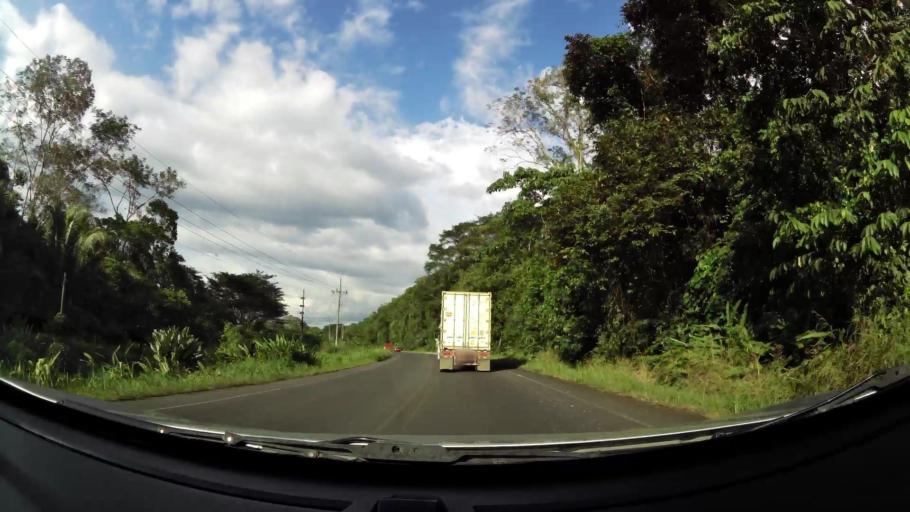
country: CR
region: Puntarenas
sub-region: Canton de Garabito
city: Jaco
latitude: 9.7726
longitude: -84.6081
